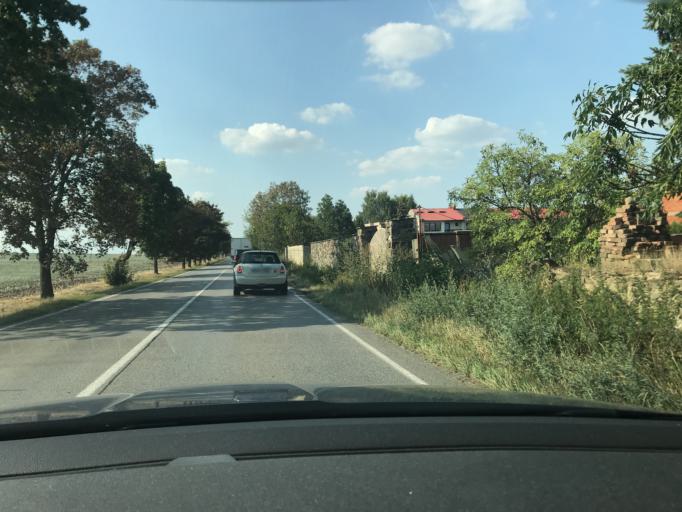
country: CZ
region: Central Bohemia
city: Velke Prilepy
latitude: 50.1926
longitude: 14.3210
